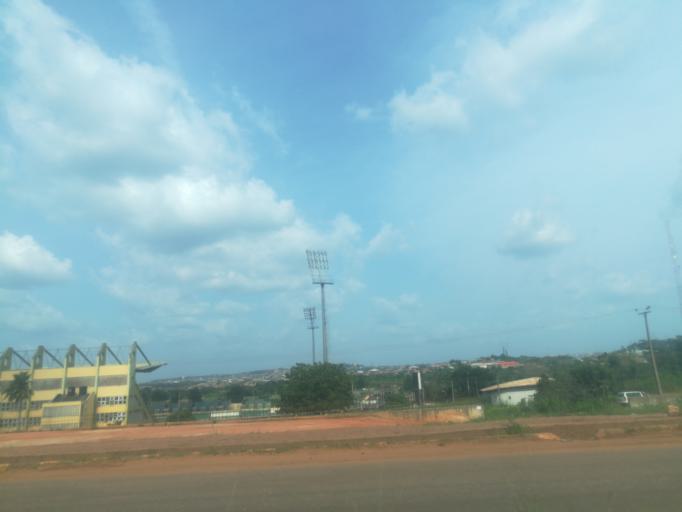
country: NG
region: Ogun
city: Abeokuta
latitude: 7.1309
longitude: 3.3542
